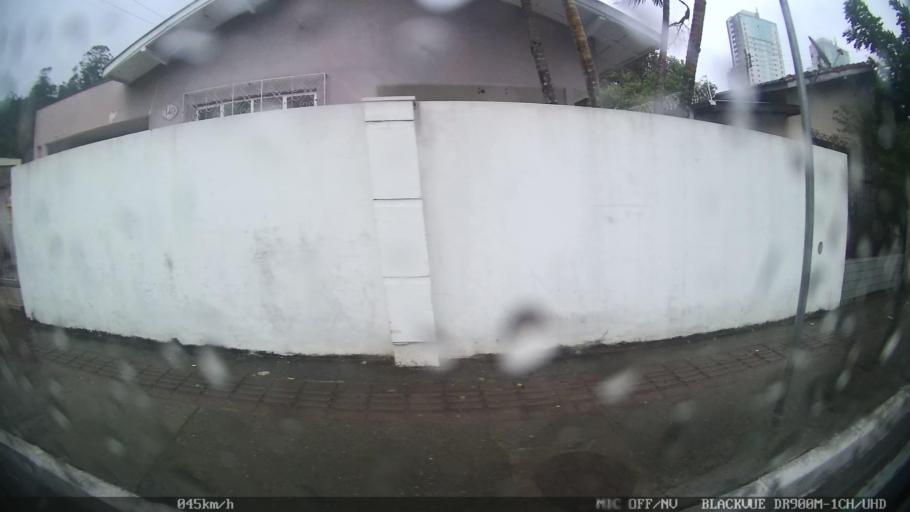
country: BR
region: Santa Catarina
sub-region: Itajai
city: Itajai
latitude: -26.9208
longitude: -48.6479
